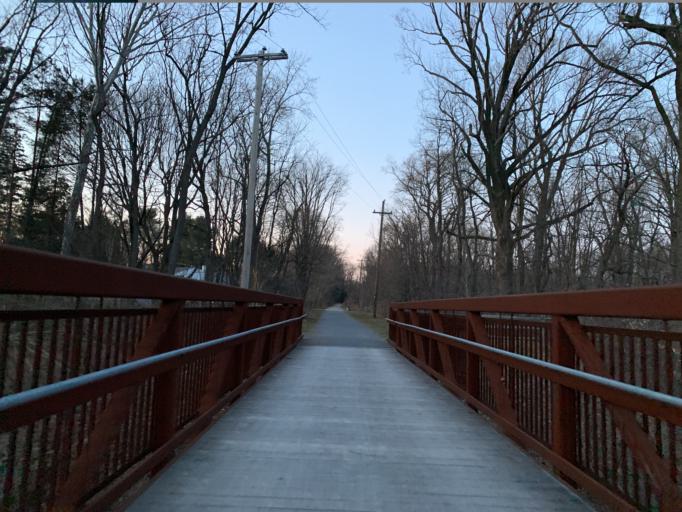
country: US
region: Pennsylvania
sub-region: Montgomery County
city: Rockledge
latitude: 40.0865
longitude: -75.0823
